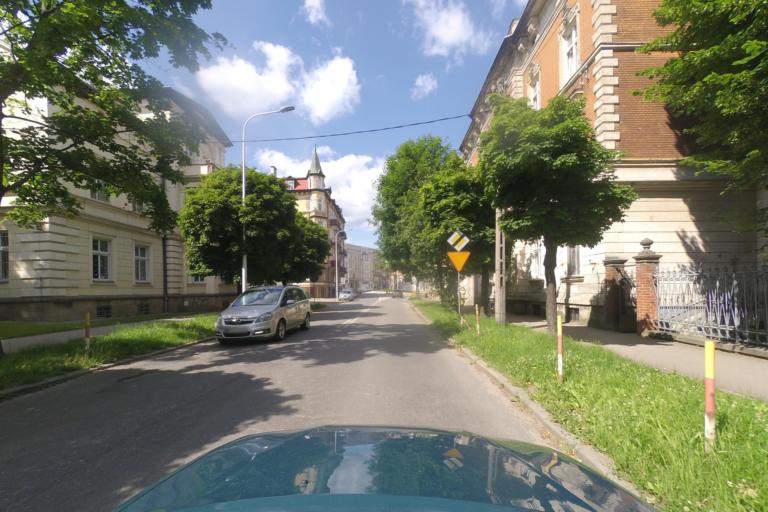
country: PL
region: Lower Silesian Voivodeship
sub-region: Powiat klodzki
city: Klodzko
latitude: 50.4351
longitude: 16.6496
